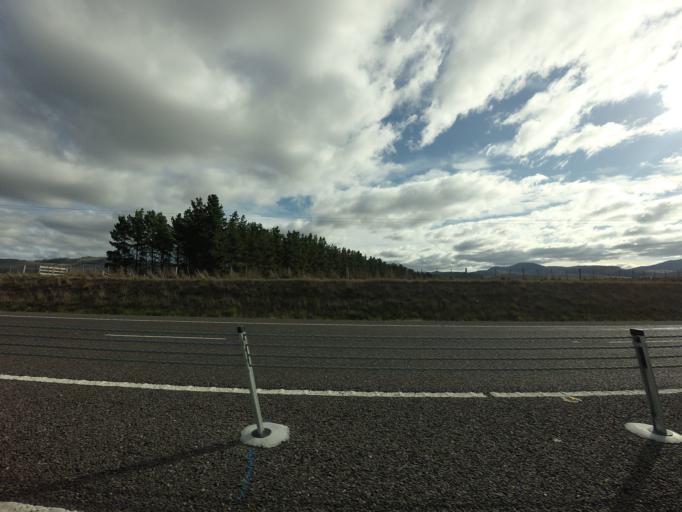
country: AU
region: Tasmania
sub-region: Brighton
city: Bridgewater
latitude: -42.5080
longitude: 147.1885
